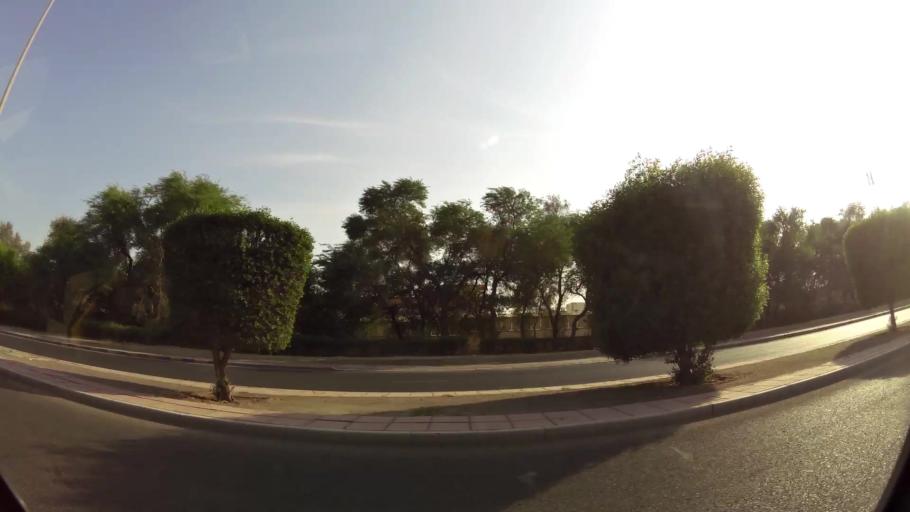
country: KW
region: Al Ahmadi
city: Ar Riqqah
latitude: 29.1655
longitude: 48.0838
